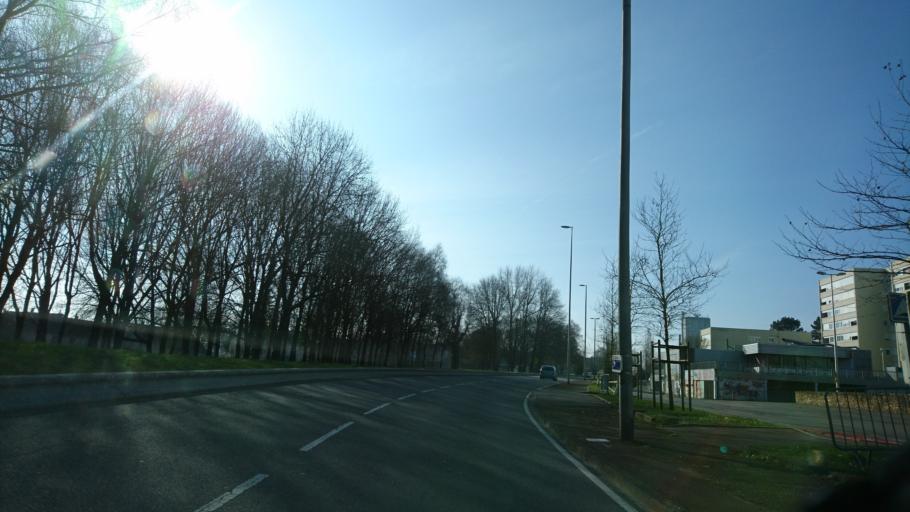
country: FR
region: Limousin
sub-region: Departement de la Haute-Vienne
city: Le Palais-sur-Vienne
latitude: 45.8775
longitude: 1.3009
